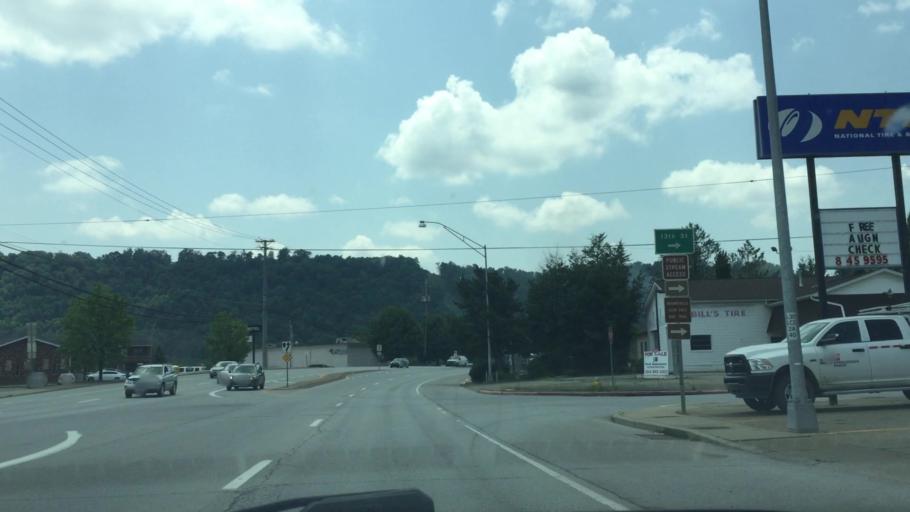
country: US
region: West Virginia
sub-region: Marshall County
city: Moundsville
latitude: 39.9124
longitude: -80.7479
